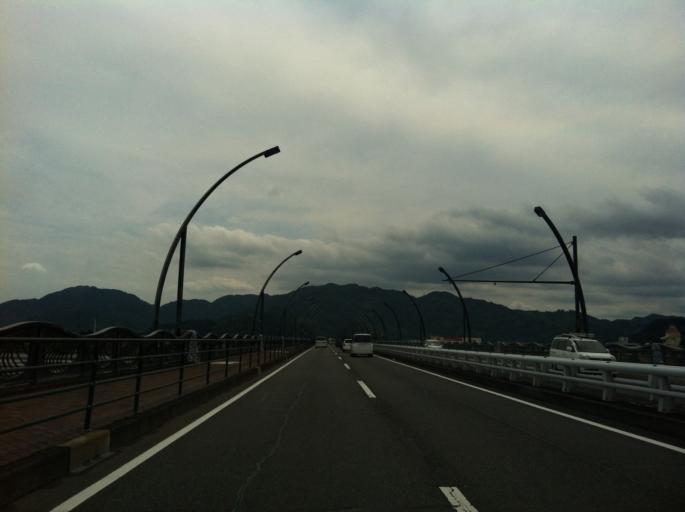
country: JP
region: Shizuoka
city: Shizuoka-shi
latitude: 34.9529
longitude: 138.3796
